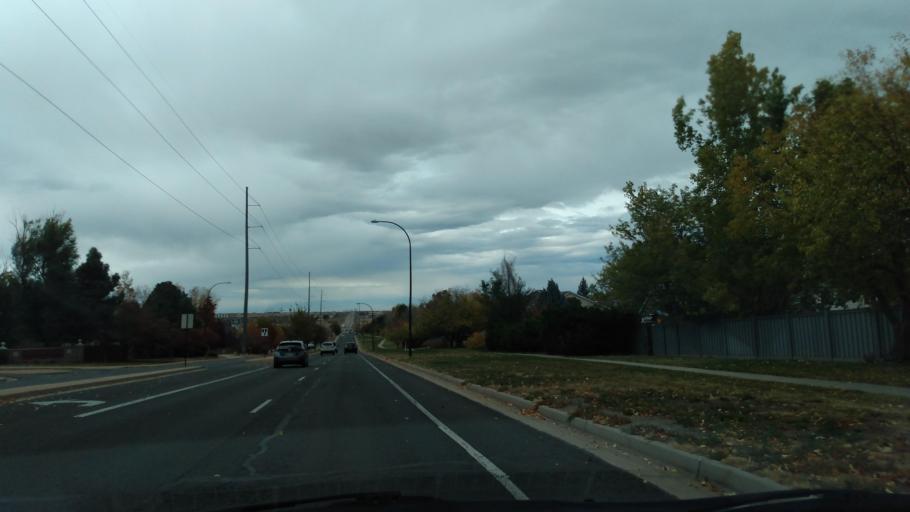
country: US
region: Colorado
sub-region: Adams County
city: Northglenn
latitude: 39.9353
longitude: -104.9780
